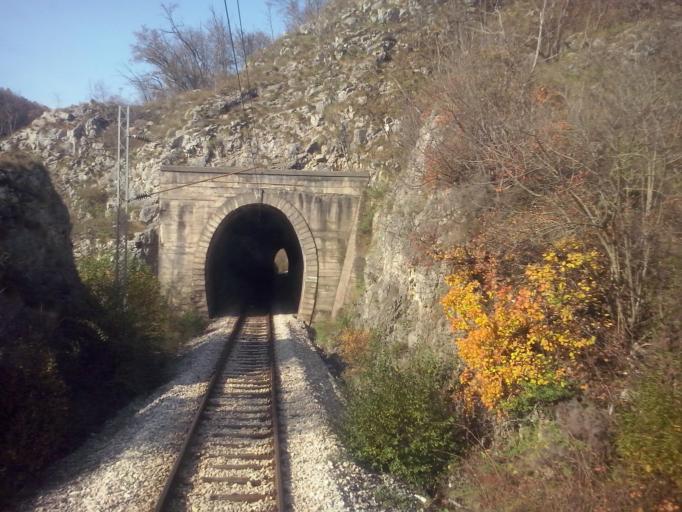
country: RS
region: Central Serbia
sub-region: Kolubarski Okrug
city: Valjevo
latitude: 44.2329
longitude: 19.8727
